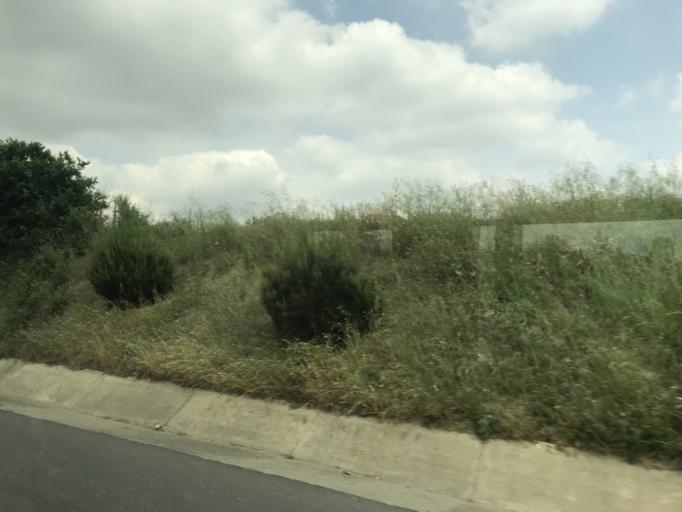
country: TR
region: Tekirdag
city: Tekirdag
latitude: 41.0022
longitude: 27.5451
